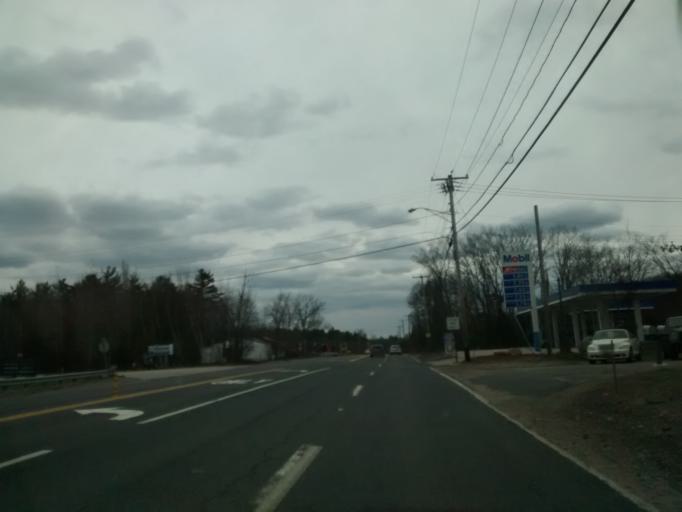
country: US
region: Massachusetts
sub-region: Worcester County
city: Oxford
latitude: 42.1630
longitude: -71.8991
